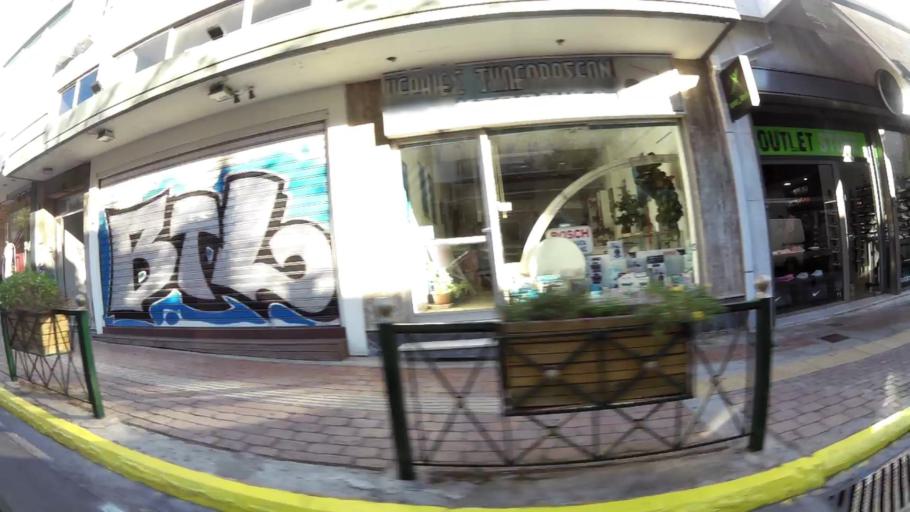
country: GR
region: Attica
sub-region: Nomarchia Athinas
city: Marousi
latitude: 38.0556
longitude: 23.8079
